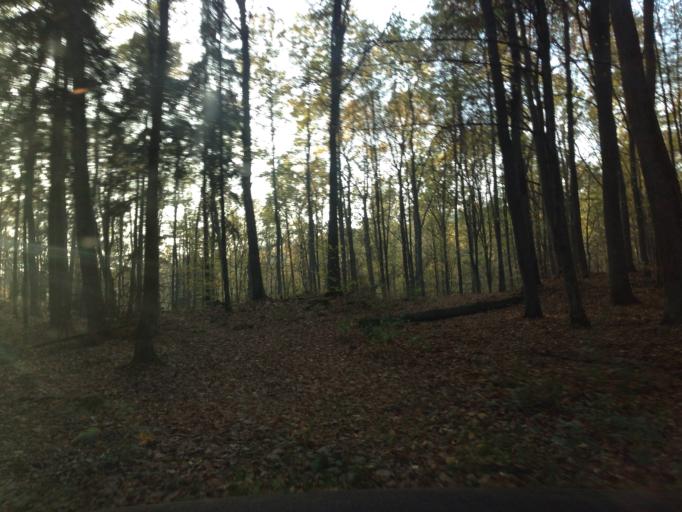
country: PL
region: Kujawsko-Pomorskie
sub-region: Powiat brodnicki
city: Gorzno
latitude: 53.2580
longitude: 19.7113
